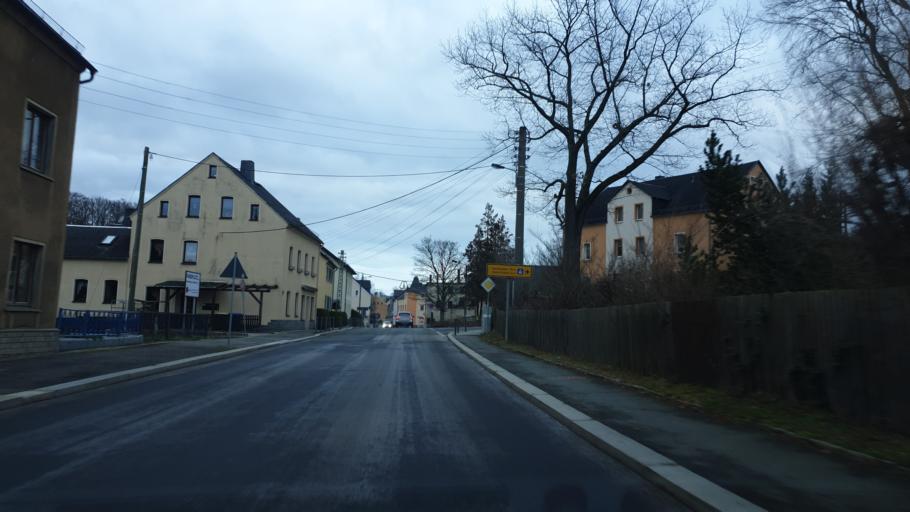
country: DE
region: Saxony
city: Bernsdorf
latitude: 50.7443
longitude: 12.6551
